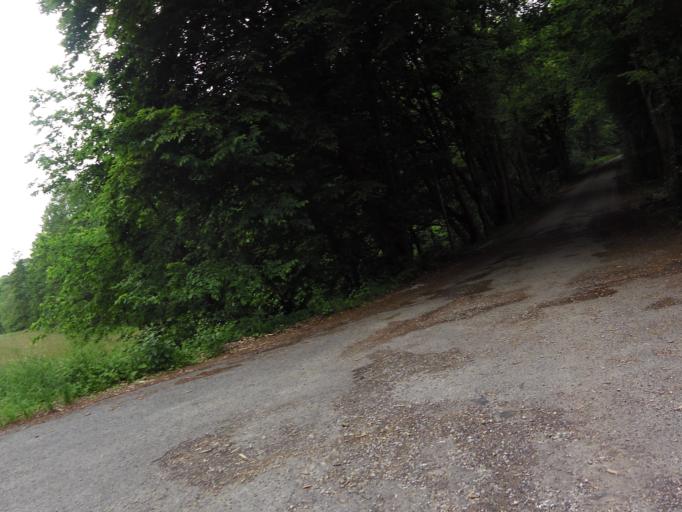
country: DE
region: Bavaria
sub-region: Regierungsbezirk Unterfranken
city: Wuerzburg
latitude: 49.7379
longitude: 9.8698
